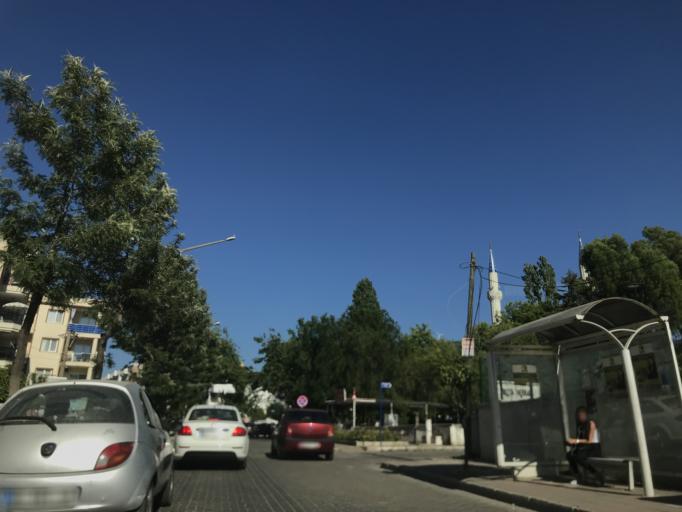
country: TR
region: Aydin
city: Davutlar
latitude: 37.7334
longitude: 27.2854
